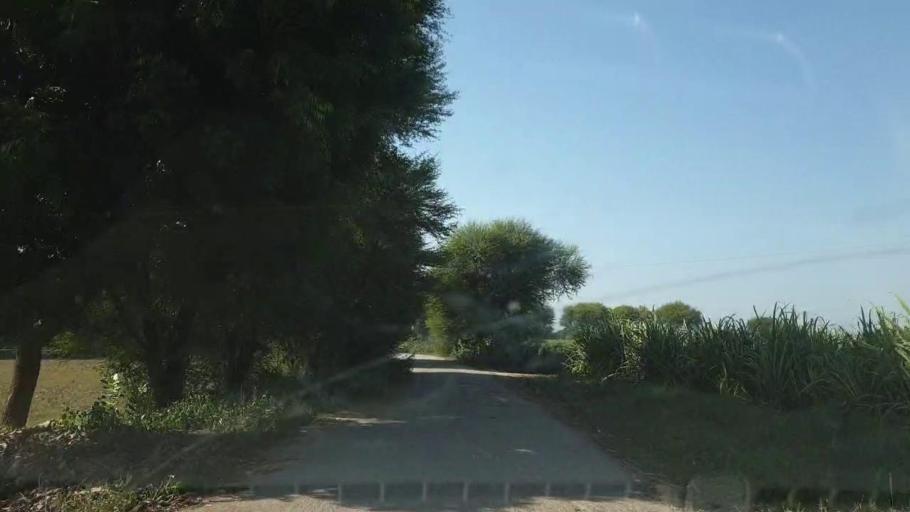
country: PK
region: Sindh
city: Tando Jam
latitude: 25.3428
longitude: 68.5852
